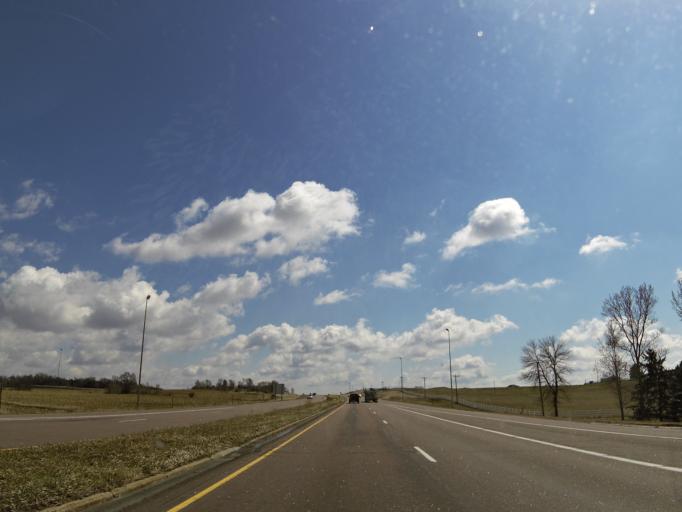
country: US
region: Minnesota
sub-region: Goodhue County
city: Cannon Falls
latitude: 44.5987
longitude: -92.9920
